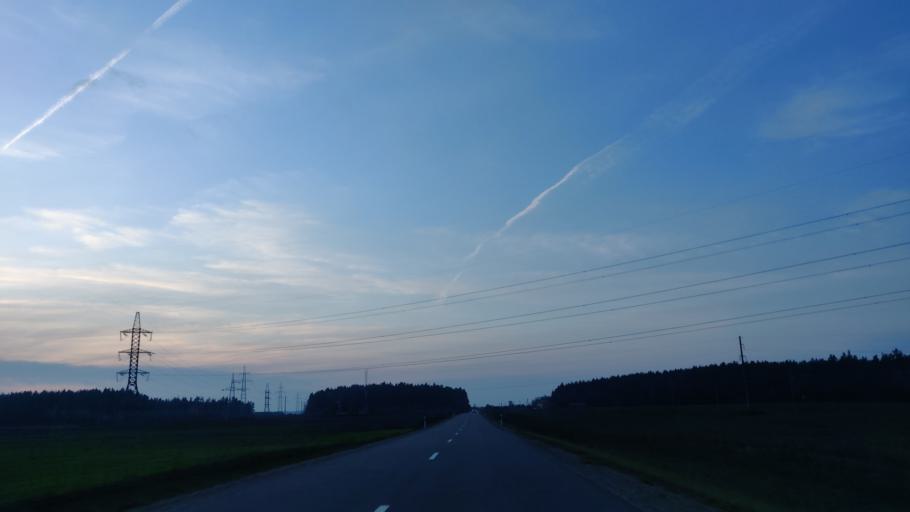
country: LT
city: Lentvaris
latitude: 54.5958
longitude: 25.0355
